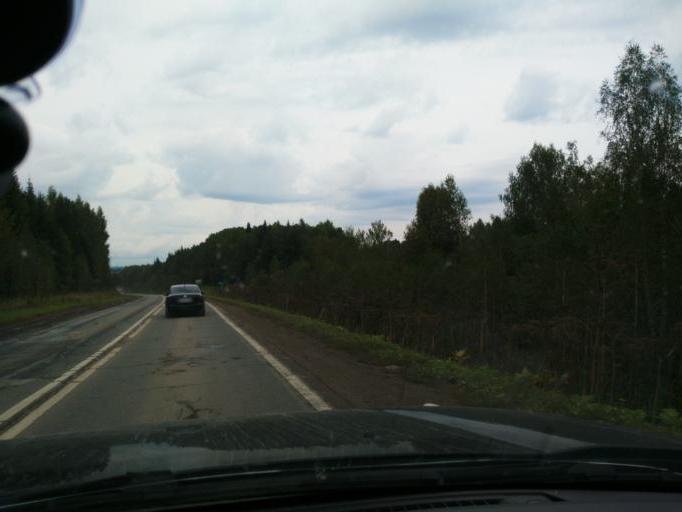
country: RU
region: Perm
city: Chernushka
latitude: 56.6842
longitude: 56.1794
